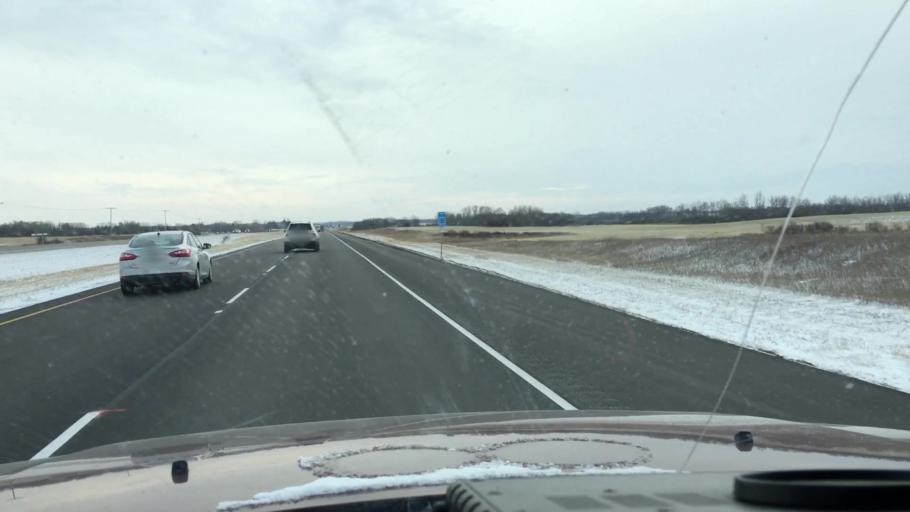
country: CA
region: Saskatchewan
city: Saskatoon
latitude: 52.0268
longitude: -106.5818
